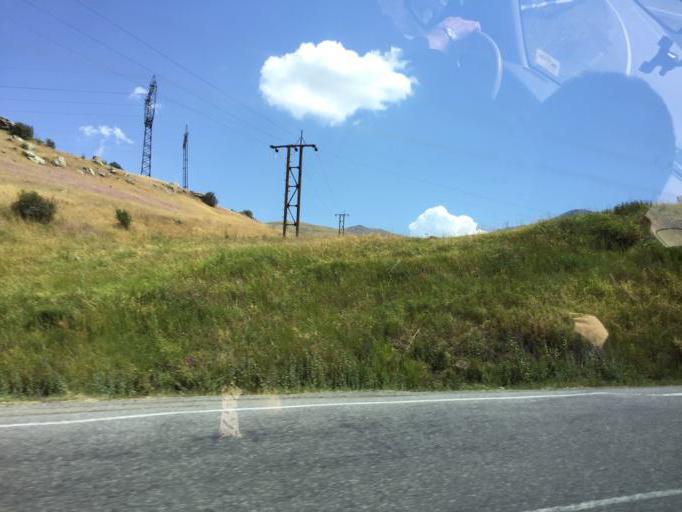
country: AM
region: Vayots' Dzori Marz
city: Jermuk
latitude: 39.7138
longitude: 45.6638
